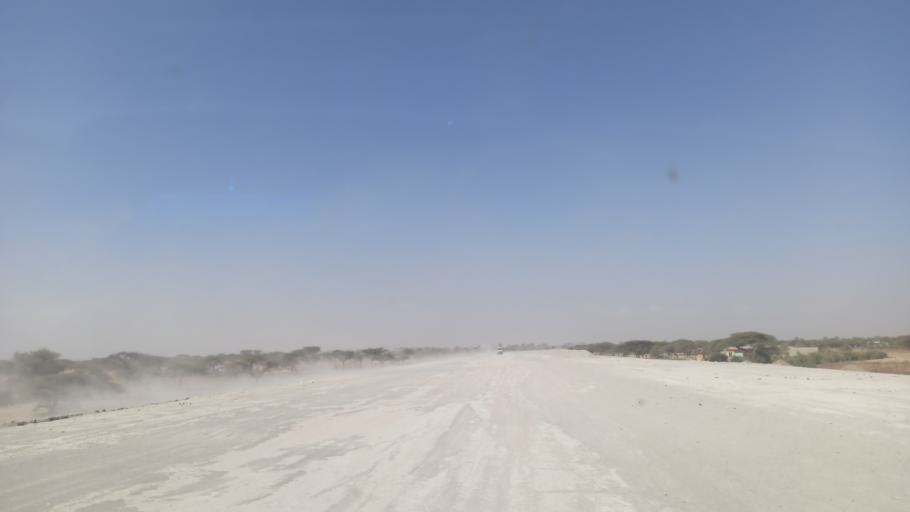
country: ET
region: Oromiya
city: Ziway
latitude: 7.6916
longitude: 38.6572
